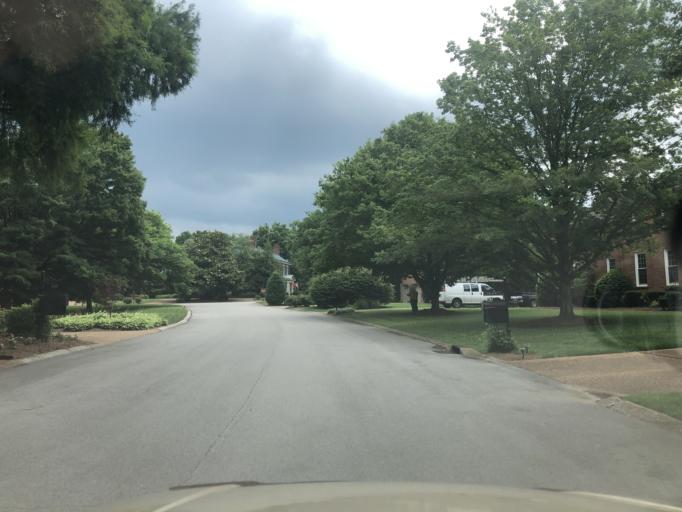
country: US
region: Tennessee
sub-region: Davidson County
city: Lakewood
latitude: 36.2368
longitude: -86.6066
